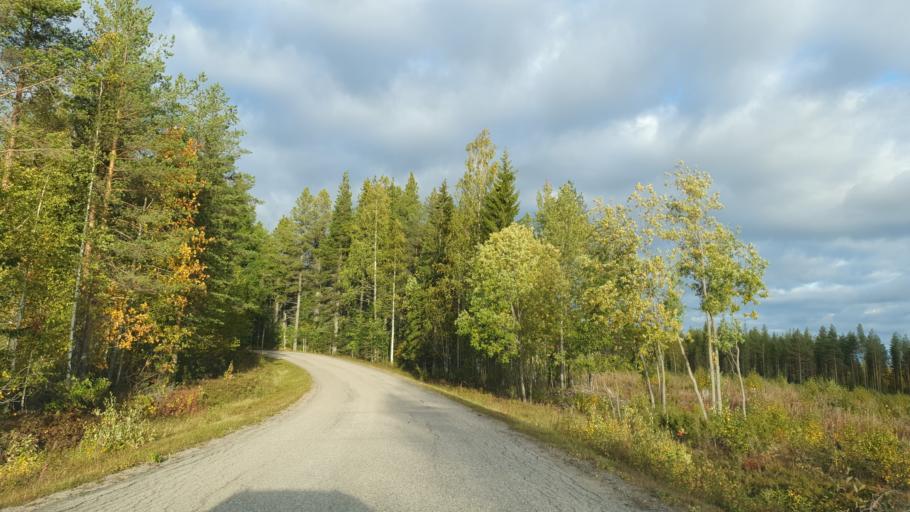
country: FI
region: North Karelia
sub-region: Pielisen Karjala
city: Lieksa
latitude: 63.9186
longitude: 30.1280
